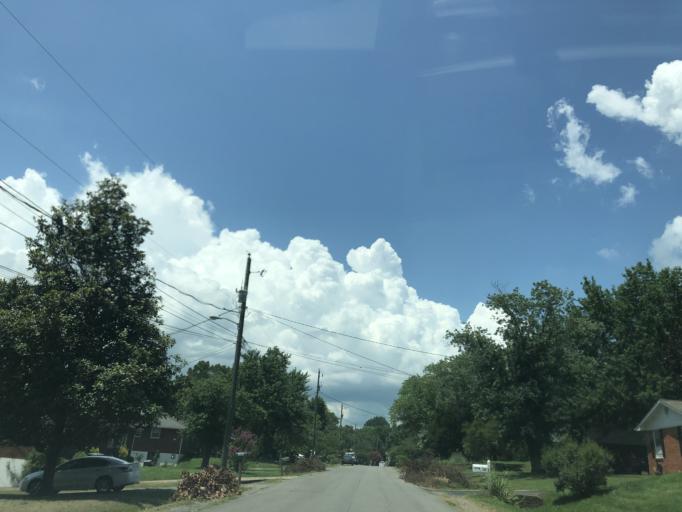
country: US
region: Tennessee
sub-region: Davidson County
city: Lakewood
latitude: 36.1972
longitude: -86.6263
